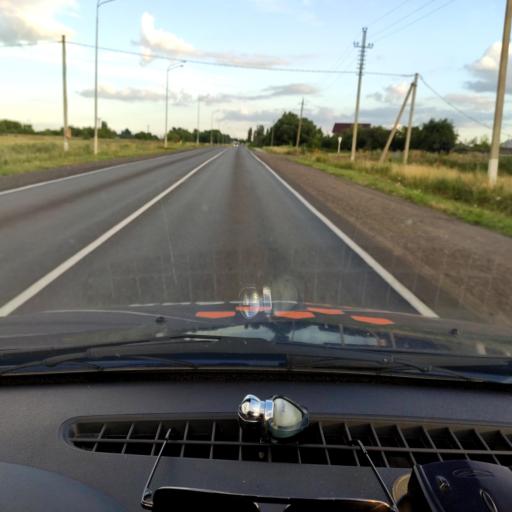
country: RU
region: Kursk
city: Gorshechnoye
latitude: 51.5329
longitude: 38.0223
